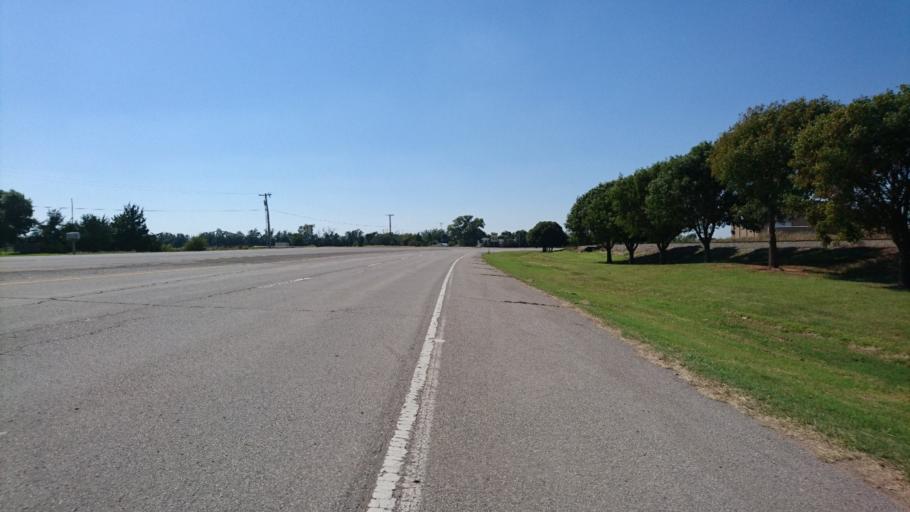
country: US
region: Oklahoma
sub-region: Custer County
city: Clinton
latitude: 35.5144
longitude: -98.9357
